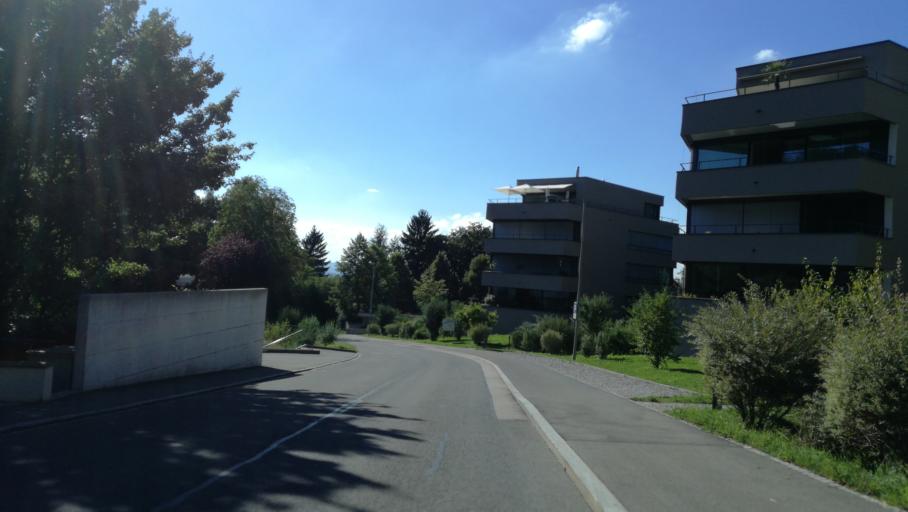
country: CH
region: Zug
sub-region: Zug
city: Zug
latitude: 47.1636
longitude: 8.5264
